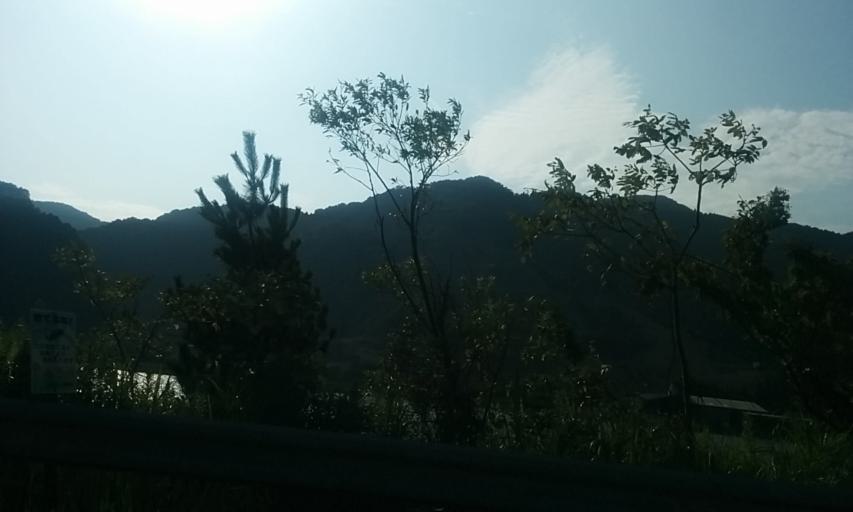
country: JP
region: Kyoto
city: Maizuru
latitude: 35.4888
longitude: 135.2856
